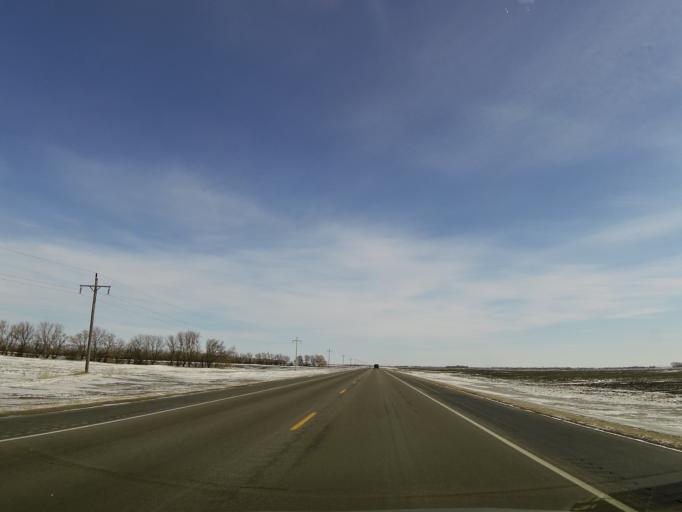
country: US
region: North Dakota
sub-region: Walsh County
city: Grafton
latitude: 48.4123
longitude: -97.3180
